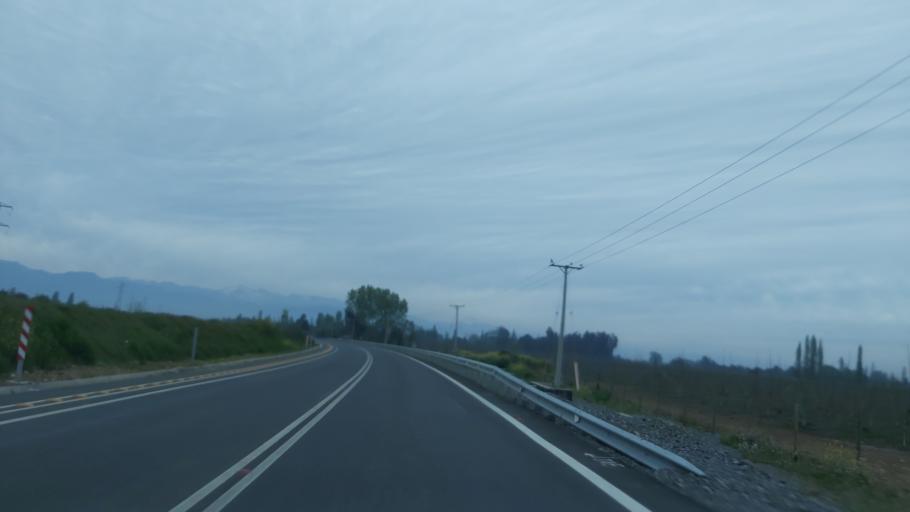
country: CL
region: Maule
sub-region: Provincia de Linares
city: Colbun
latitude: -35.7052
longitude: -71.4845
